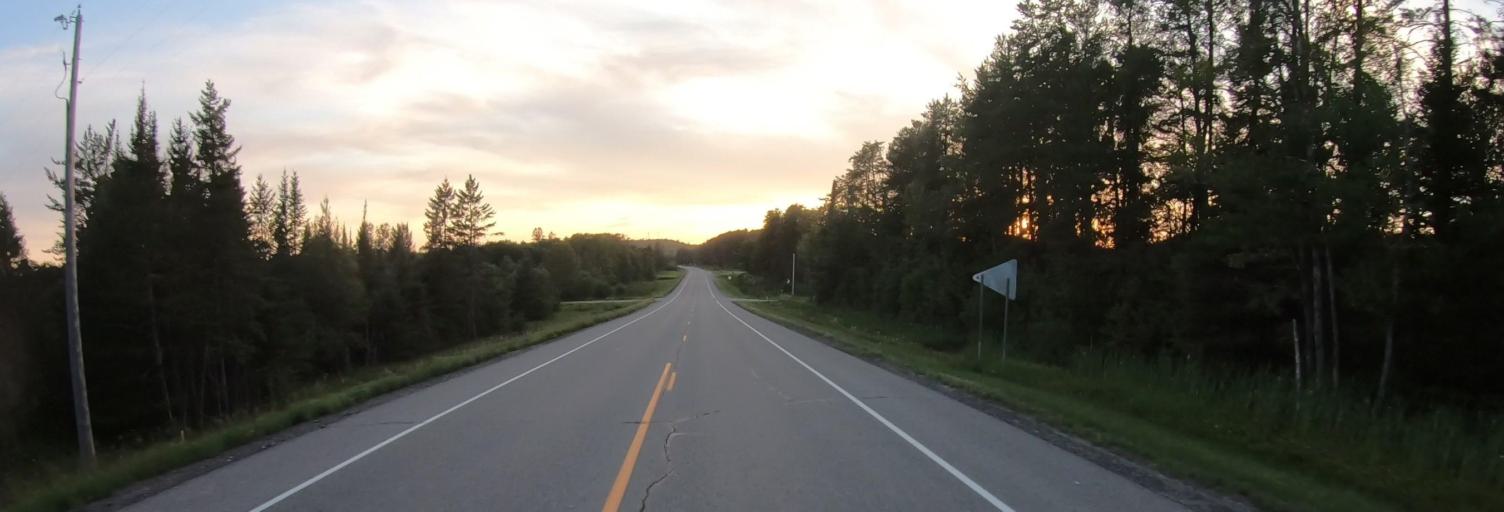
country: US
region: Minnesota
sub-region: Saint Louis County
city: Aurora
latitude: 47.8131
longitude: -92.2339
